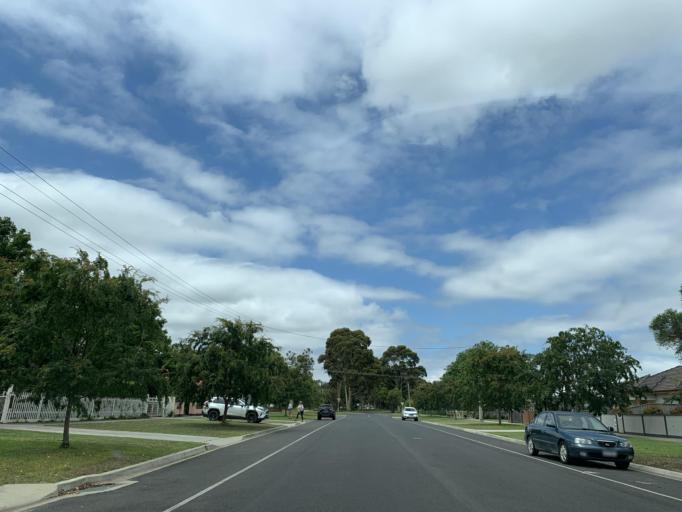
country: AU
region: Victoria
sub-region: Wellington
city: Sale
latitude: -38.1070
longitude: 147.0755
